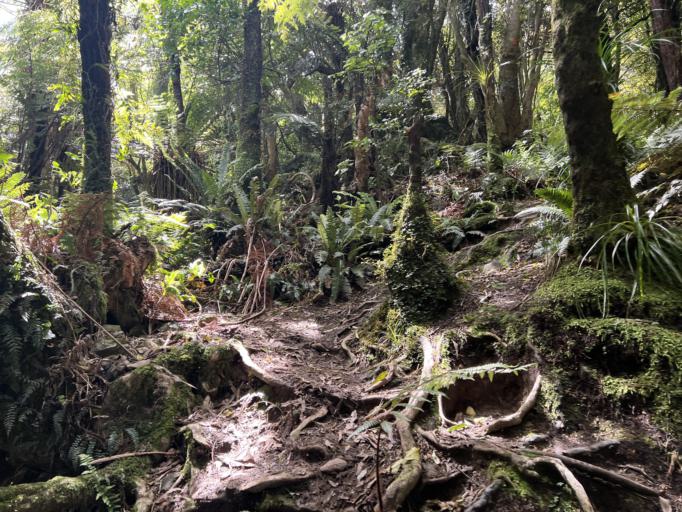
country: NZ
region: Wellington
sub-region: Kapiti Coast District
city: Paraparaumu
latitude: -40.8789
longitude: 175.0912
